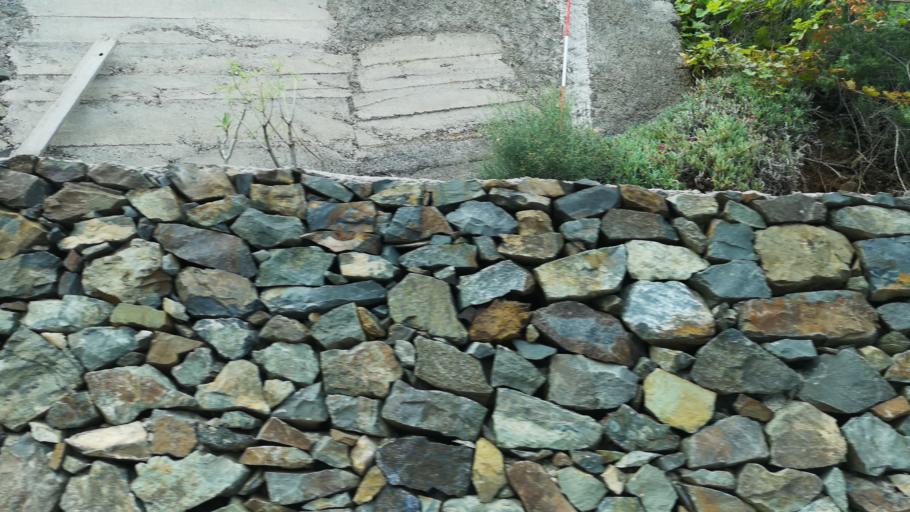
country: ES
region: Canary Islands
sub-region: Provincia de Santa Cruz de Tenerife
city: Vallehermosa
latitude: 28.1996
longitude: -17.2564
